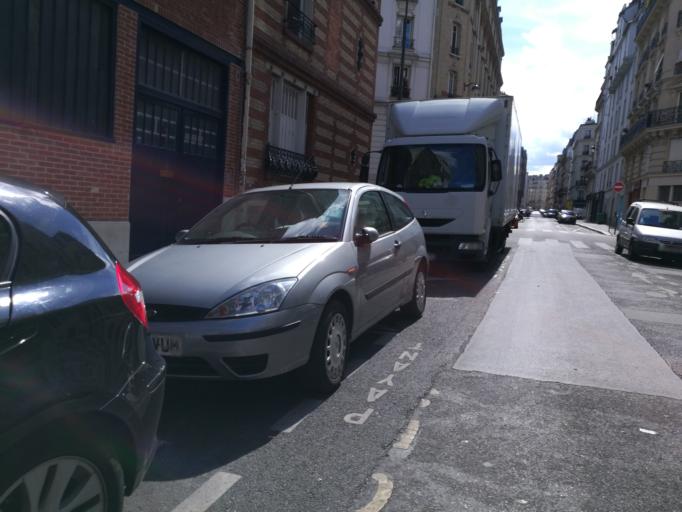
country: FR
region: Ile-de-France
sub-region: Paris
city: Saint-Ouen
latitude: 48.8941
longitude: 2.3395
